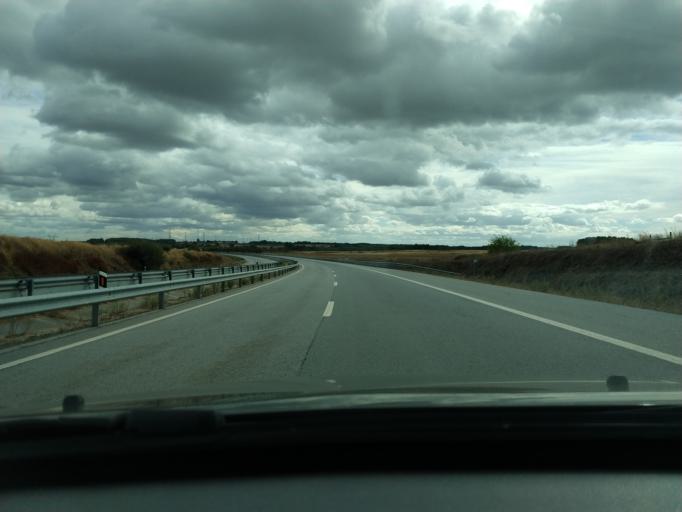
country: PT
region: Guarda
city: Alcains
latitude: 40.0148
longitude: -7.4668
